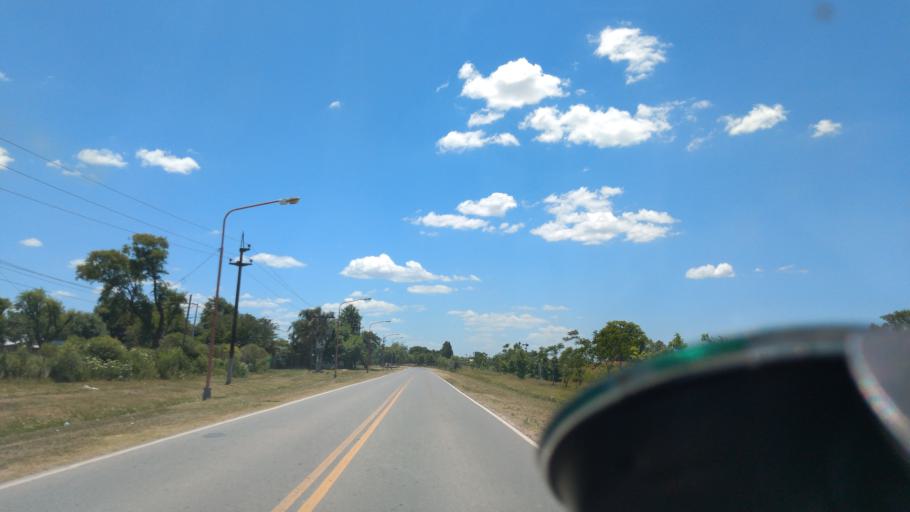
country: AR
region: Santa Fe
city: Laguna Paiva
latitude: -31.3174
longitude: -60.6585
